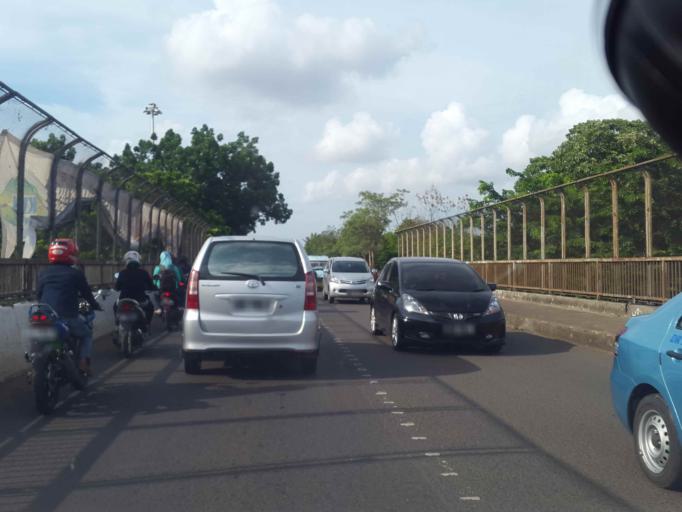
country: ID
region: Jakarta Raya
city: Jakarta
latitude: -6.2568
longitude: 106.9099
